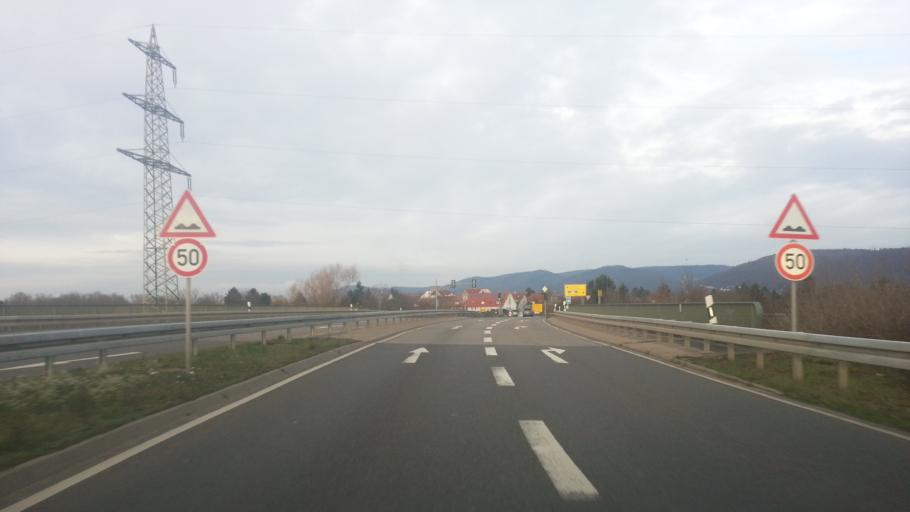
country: DE
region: Baden-Wuerttemberg
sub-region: Karlsruhe Region
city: Sandhausen
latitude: 49.3694
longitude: 8.6609
